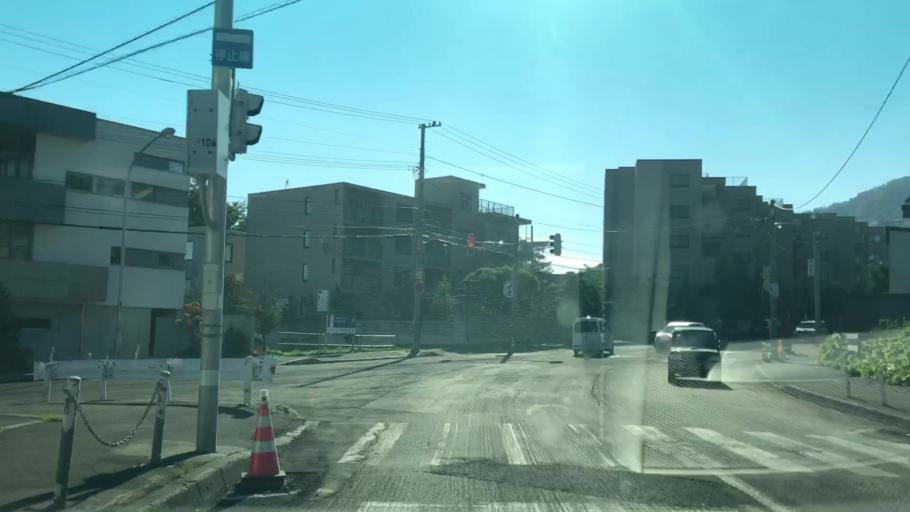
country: JP
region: Hokkaido
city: Sapporo
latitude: 43.0422
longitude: 141.3196
